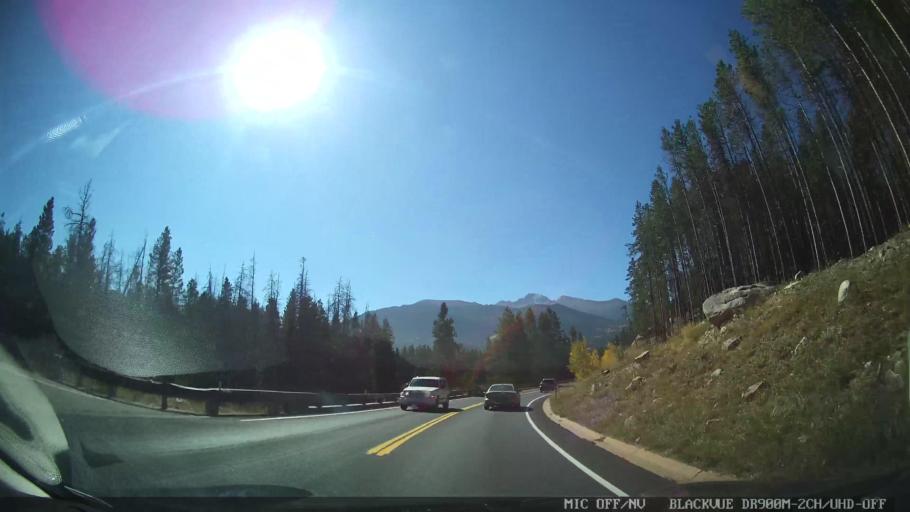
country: US
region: Colorado
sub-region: Larimer County
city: Estes Park
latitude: 40.3343
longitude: -105.5988
